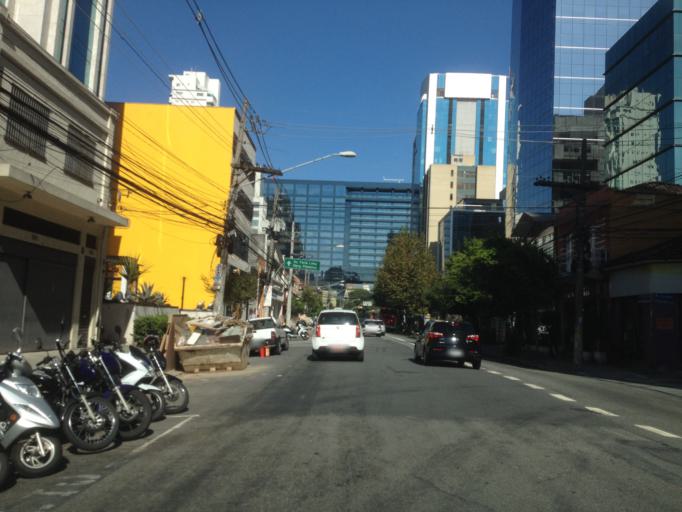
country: BR
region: Sao Paulo
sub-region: Sao Paulo
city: Sao Paulo
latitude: -23.5855
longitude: -46.6784
